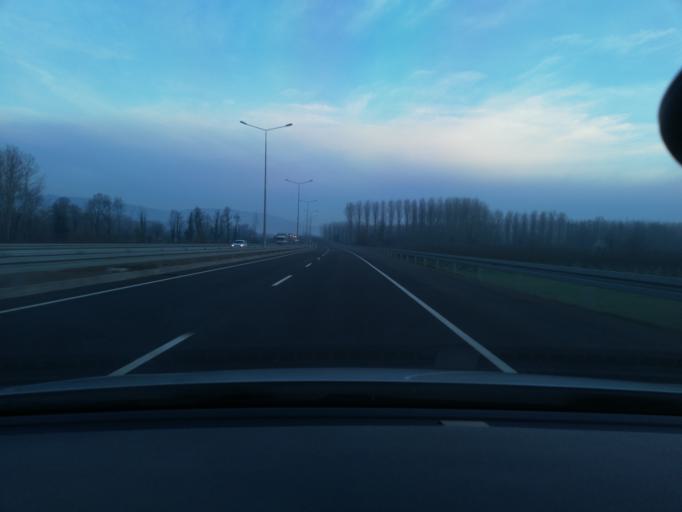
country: TR
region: Duzce
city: Duzce
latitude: 40.8119
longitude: 31.1692
